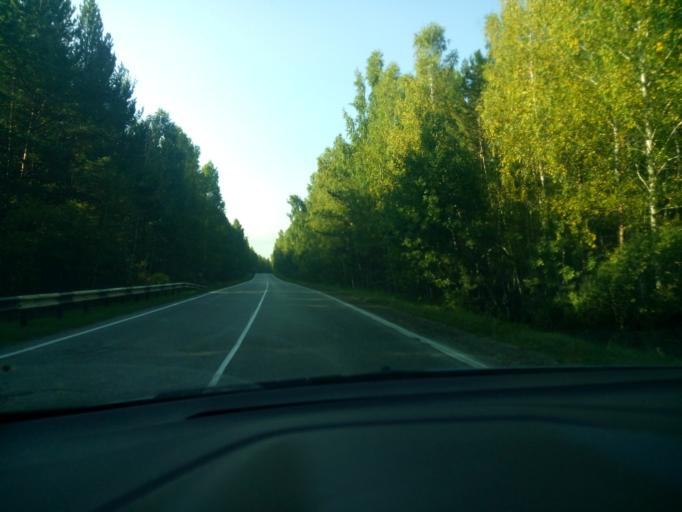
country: RU
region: Chelyabinsk
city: Ozersk
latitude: 55.8491
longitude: 60.6570
